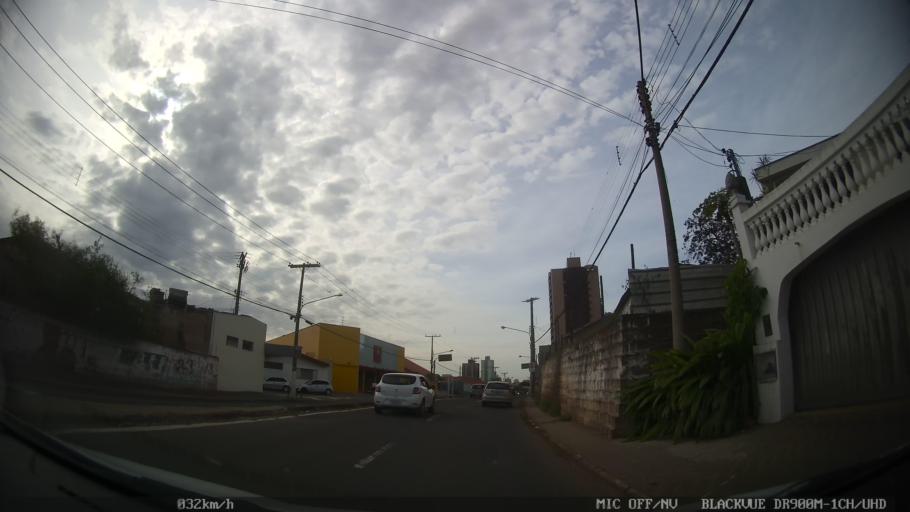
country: BR
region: Sao Paulo
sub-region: Piracicaba
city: Piracicaba
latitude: -22.7397
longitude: -47.6412
